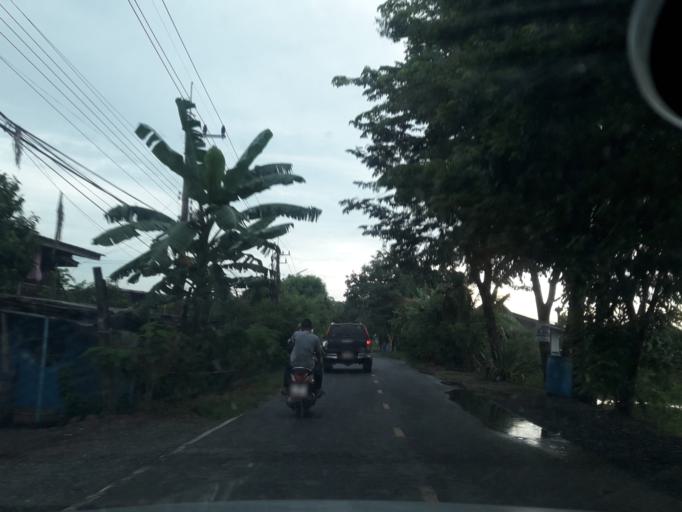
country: TH
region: Phra Nakhon Si Ayutthaya
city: Wang Noi
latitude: 14.2581
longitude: 100.7858
